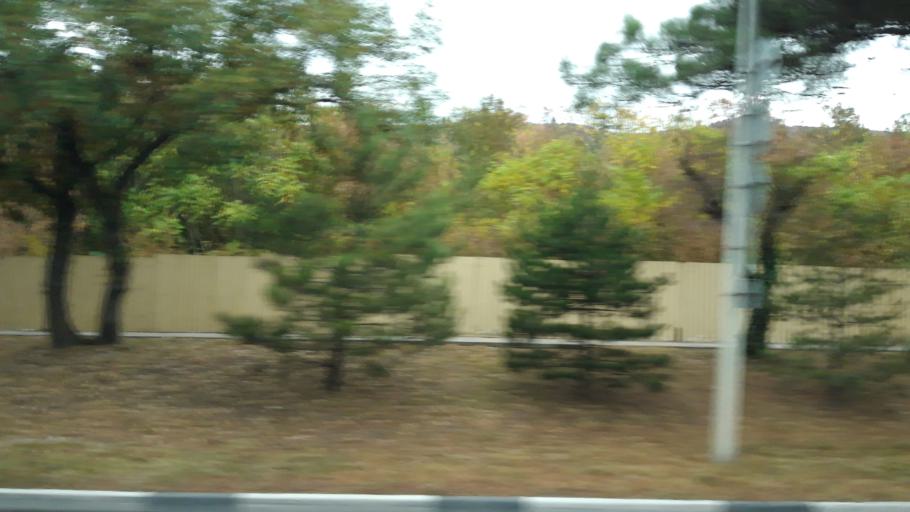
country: RU
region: Krasnodarskiy
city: Gelendzhik
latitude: 44.5824
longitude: 38.0627
